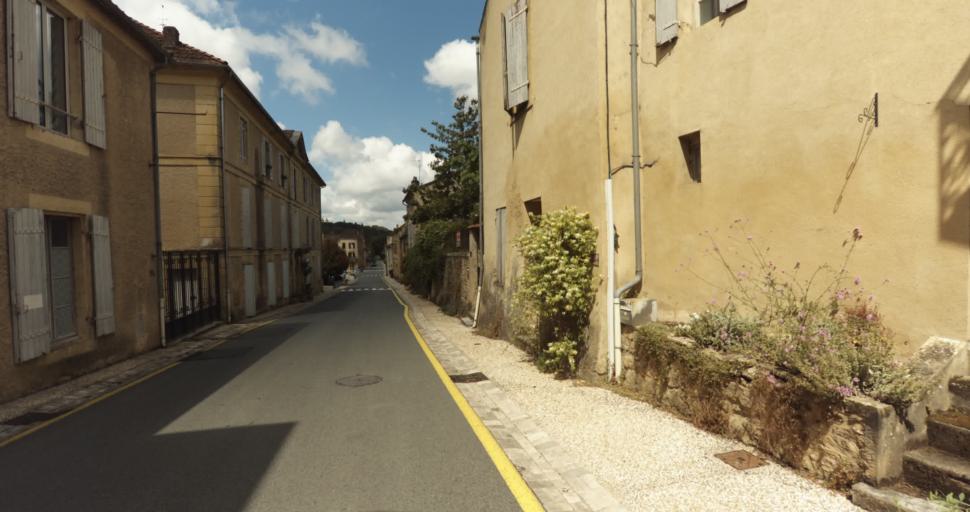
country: FR
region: Aquitaine
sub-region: Departement de la Dordogne
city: Beaumont-du-Perigord
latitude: 44.8119
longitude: 0.8747
